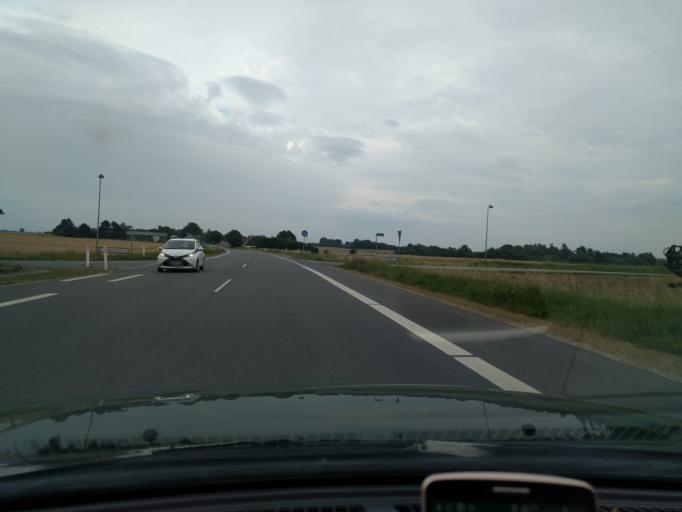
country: DK
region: Zealand
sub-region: Slagelse Kommune
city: Skaelskor
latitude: 55.2492
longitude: 11.3618
